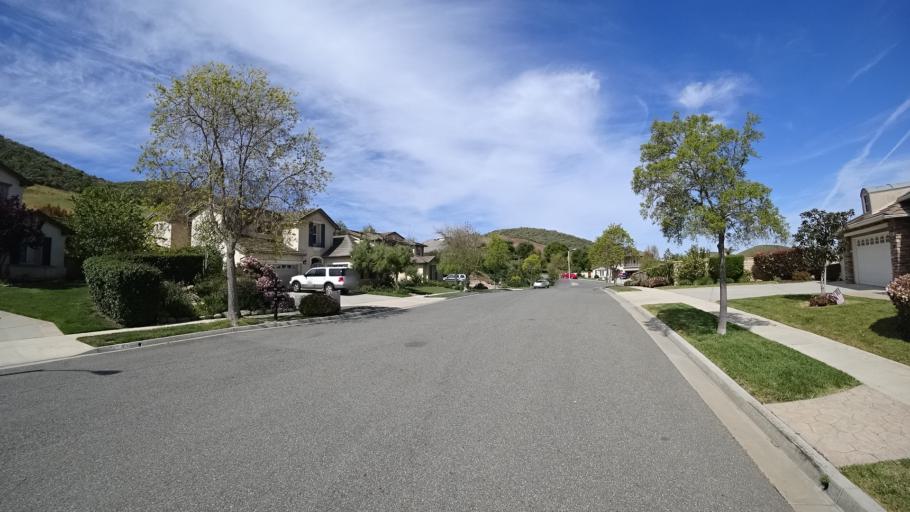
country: US
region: California
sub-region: Ventura County
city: Casa Conejo
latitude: 34.1709
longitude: -118.9806
